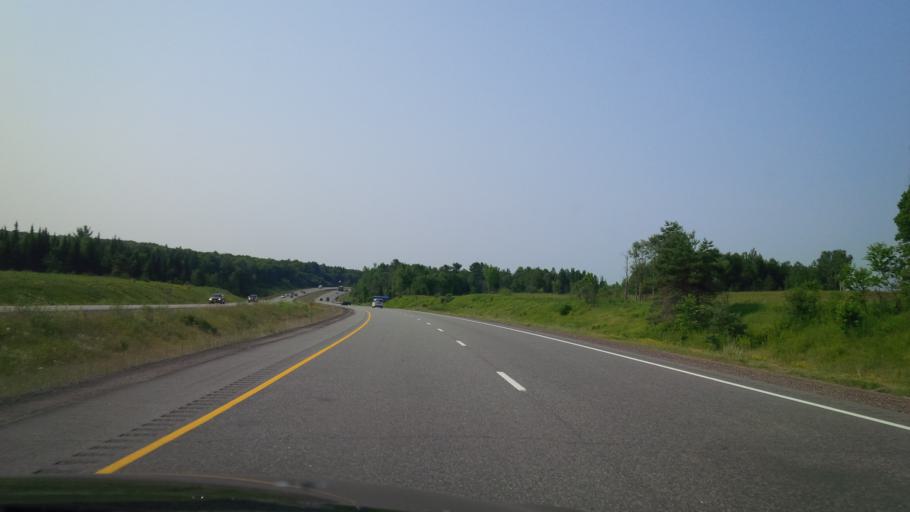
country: CA
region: Ontario
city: Bracebridge
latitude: 45.0329
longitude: -79.2931
